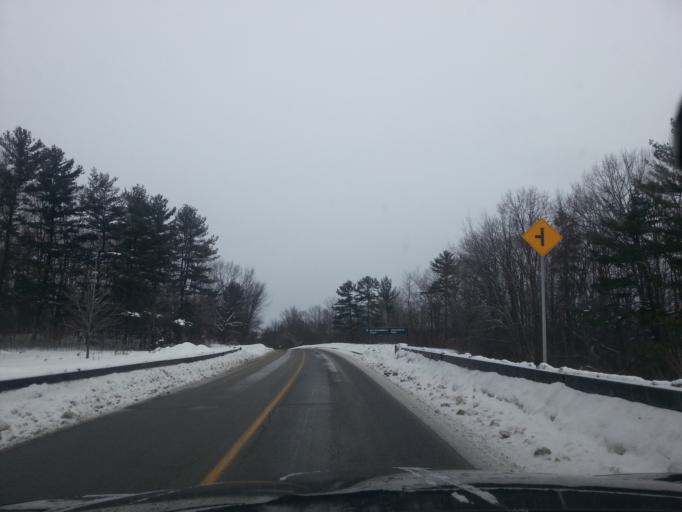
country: CA
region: Ontario
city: Ottawa
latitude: 45.4332
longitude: -75.7503
